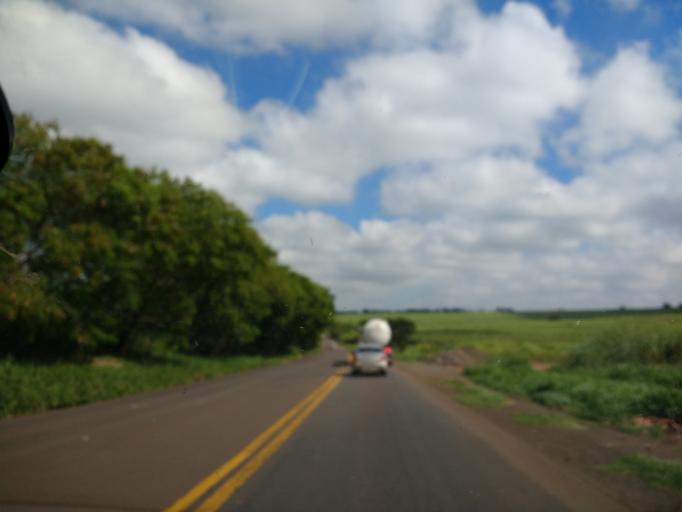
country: BR
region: Parana
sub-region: Cruzeiro Do Oeste
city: Cruzeiro do Oeste
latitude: -23.7637
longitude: -53.0008
